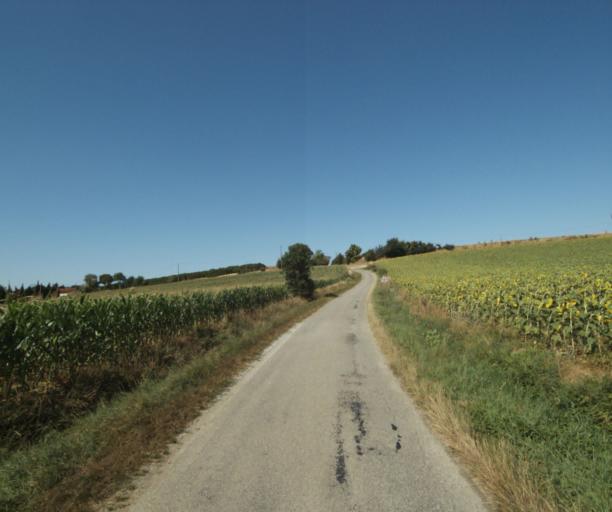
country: FR
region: Midi-Pyrenees
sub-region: Departement de la Haute-Garonne
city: Saint-Felix-Lauragais
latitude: 43.4792
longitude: 1.8957
